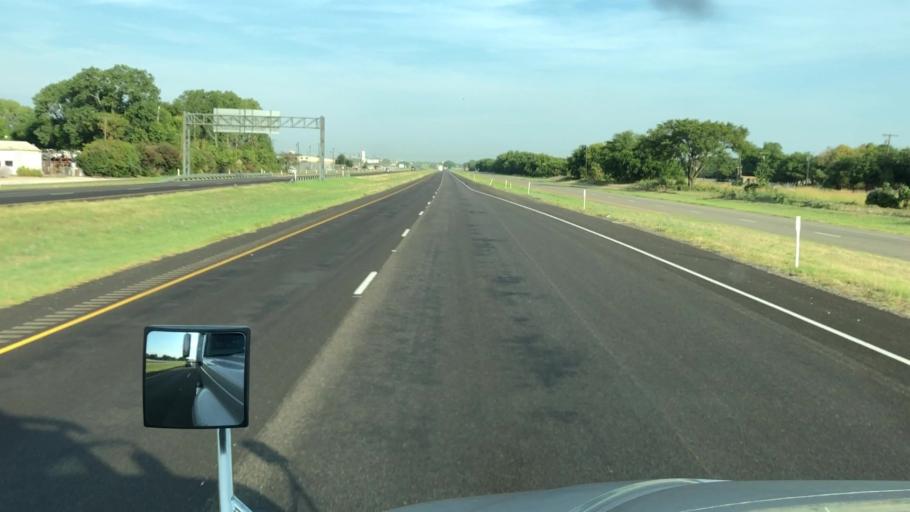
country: US
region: Texas
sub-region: McLennan County
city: Bellmead
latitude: 31.5489
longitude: -97.0748
